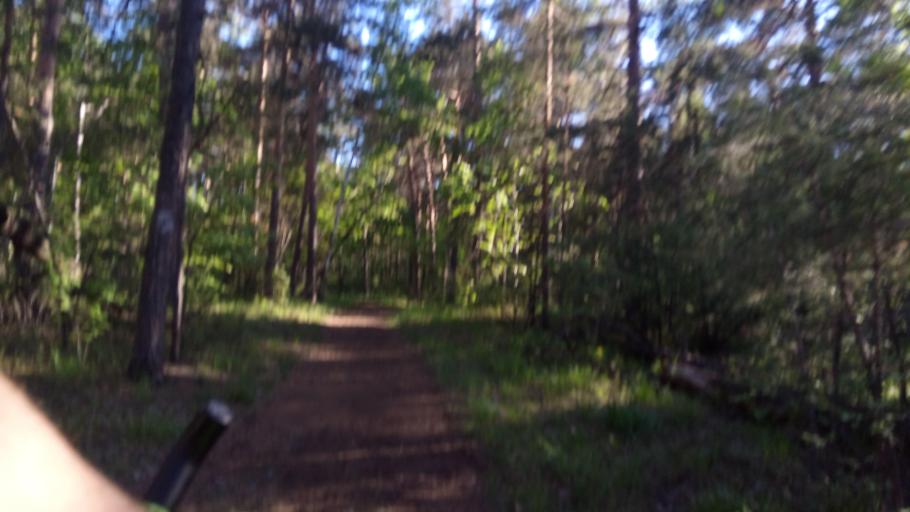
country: RU
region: Chelyabinsk
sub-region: Gorod Chelyabinsk
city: Chelyabinsk
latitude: 55.1315
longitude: 61.3353
